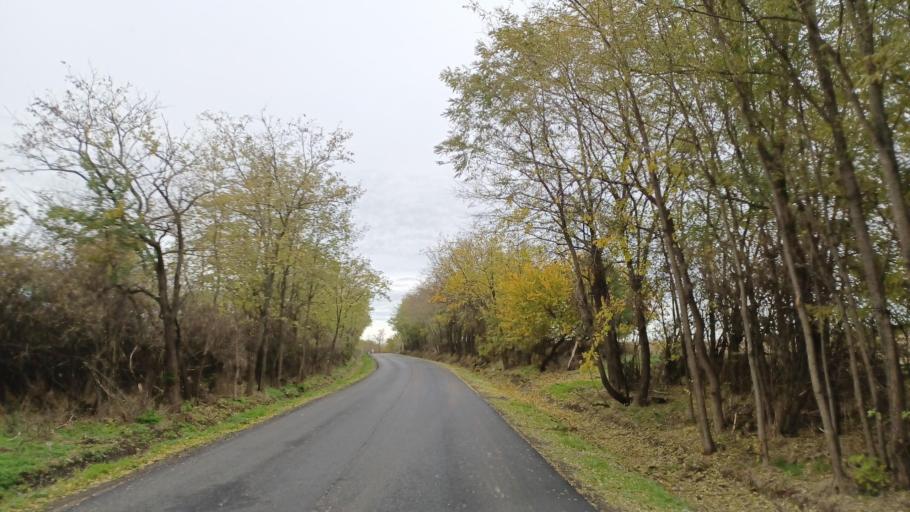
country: HU
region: Tolna
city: Tengelic
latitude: 46.5386
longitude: 18.7577
